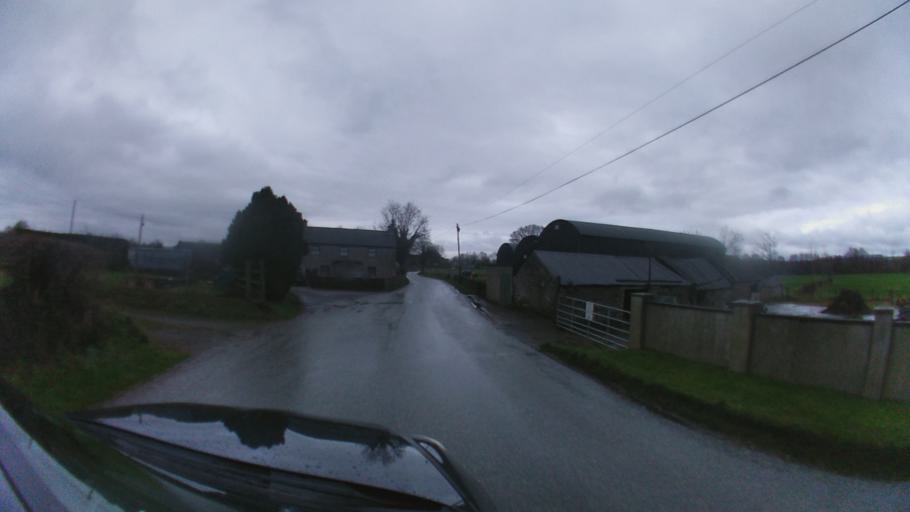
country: IE
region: Leinster
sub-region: County Carlow
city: Bagenalstown
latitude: 52.6449
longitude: -6.9902
